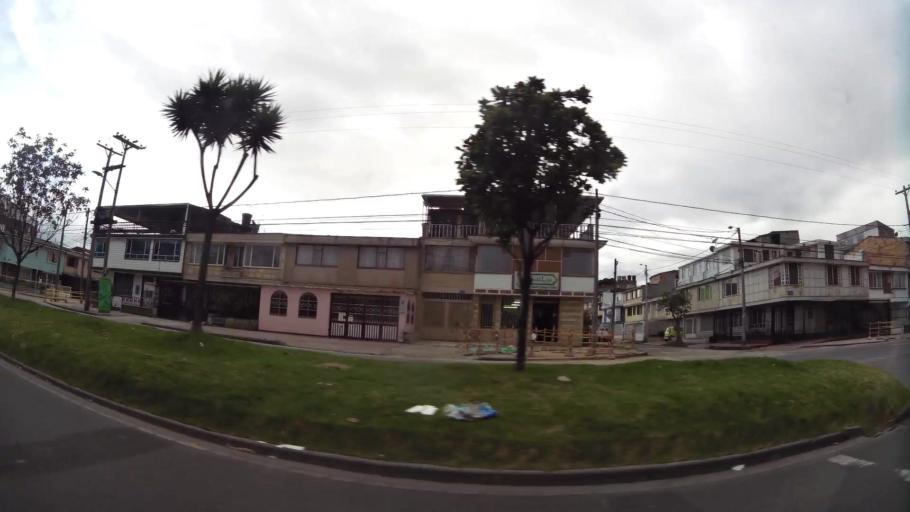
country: CO
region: Bogota D.C.
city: Bogota
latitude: 4.5970
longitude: -74.1050
